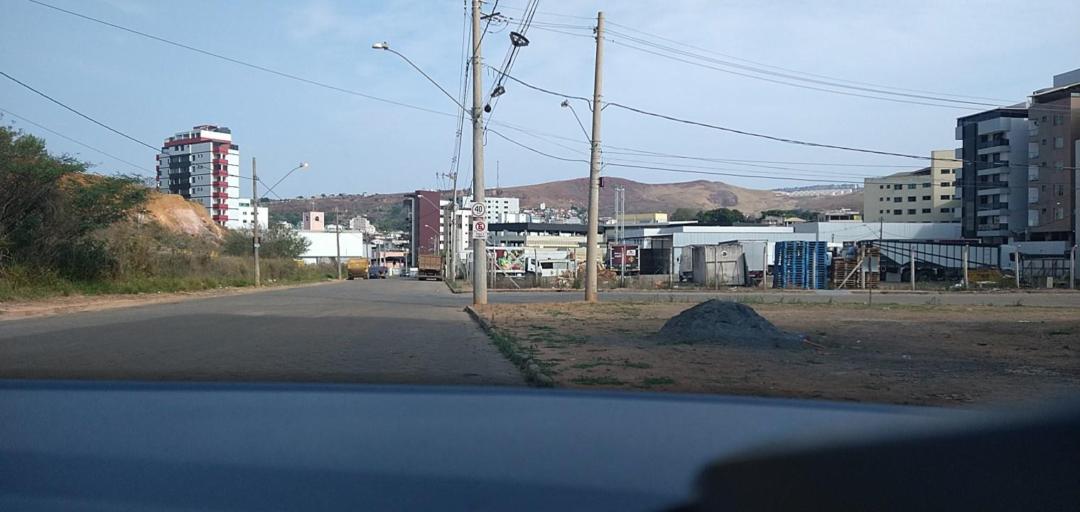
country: BR
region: Minas Gerais
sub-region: Joao Monlevade
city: Joao Monlevade
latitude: -19.8052
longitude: -43.1845
